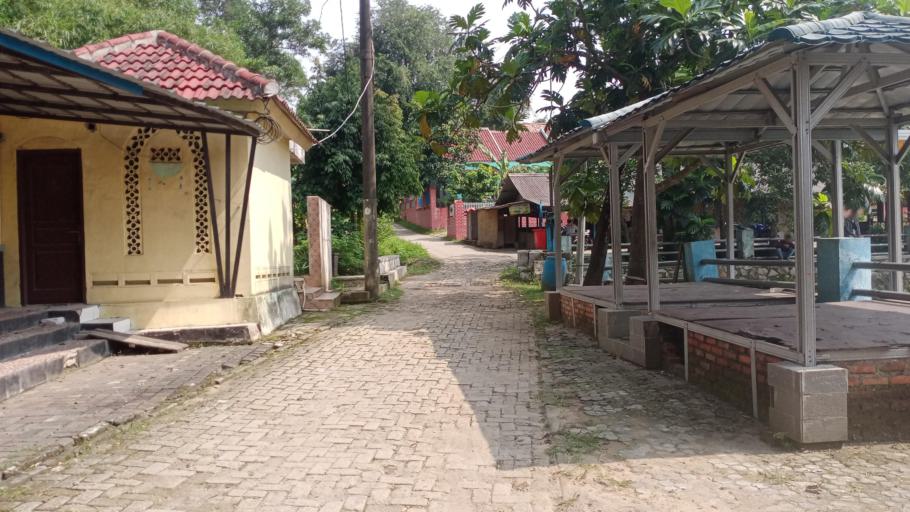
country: ID
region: West Java
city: Cikarang
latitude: -6.3440
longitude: 107.1855
